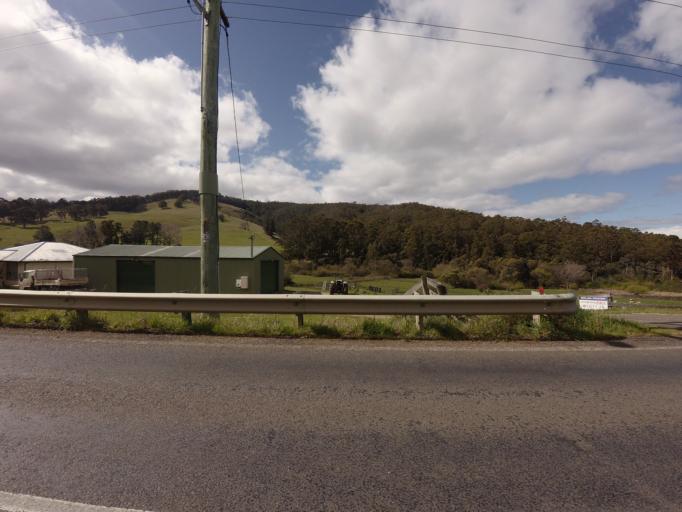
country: AU
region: Tasmania
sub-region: Huon Valley
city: Cygnet
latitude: -43.3101
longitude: 147.0133
